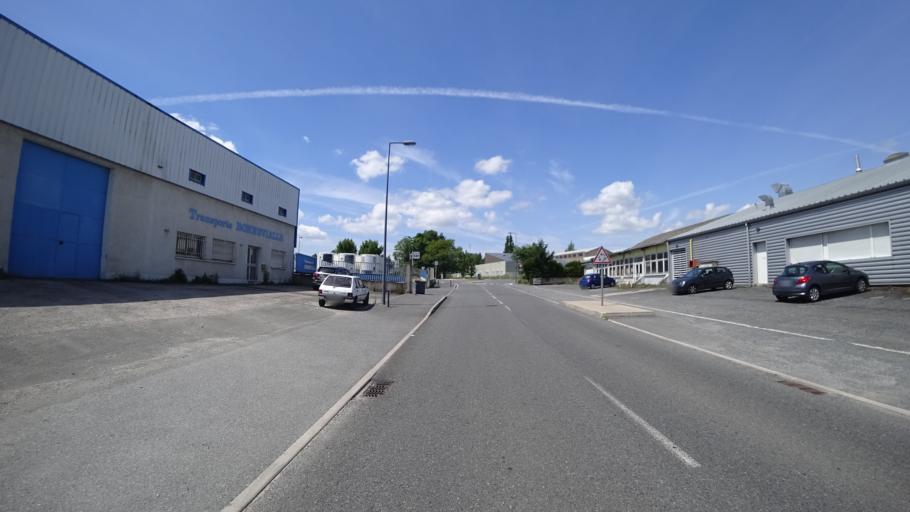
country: FR
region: Midi-Pyrenees
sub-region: Departement de l'Aveyron
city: Rodez
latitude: 44.3592
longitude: 2.5945
